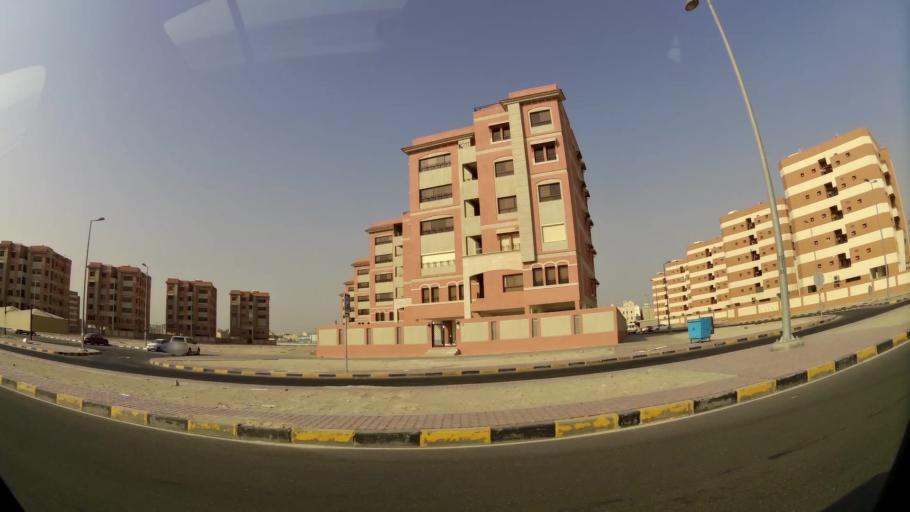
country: KW
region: Al Asimah
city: Ar Rabiyah
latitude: 29.3311
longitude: 47.8160
